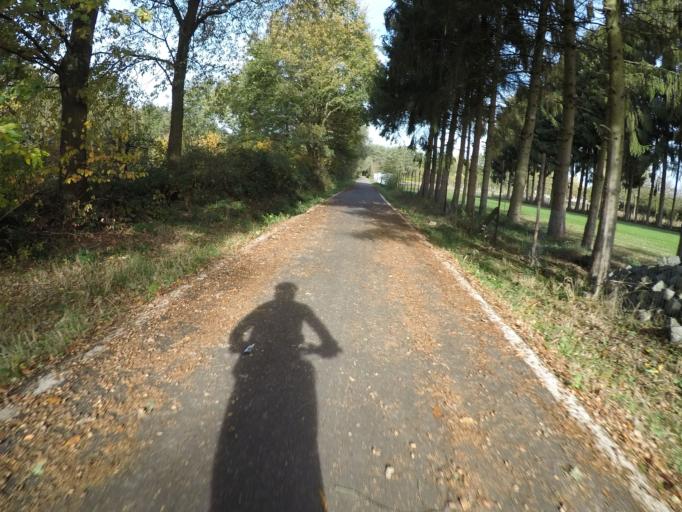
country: BE
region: Flanders
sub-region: Provincie Vlaams-Brabant
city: Begijnendijk
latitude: 51.0003
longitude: 4.7925
